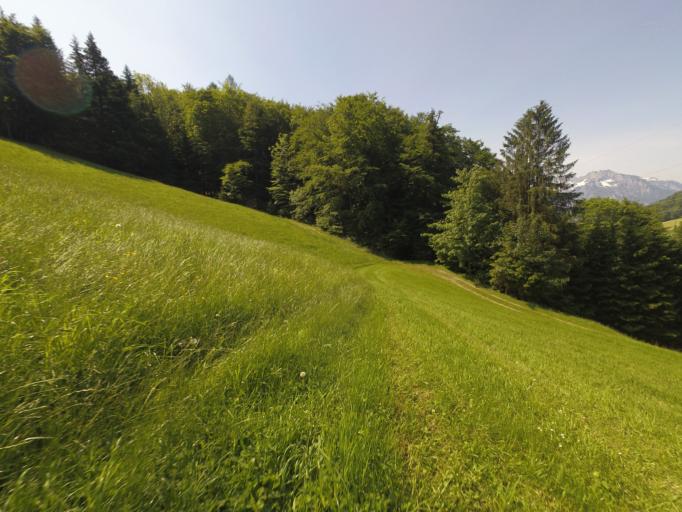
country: AT
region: Salzburg
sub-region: Politischer Bezirk Salzburg-Umgebung
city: Koppl
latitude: 47.7824
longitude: 13.1280
